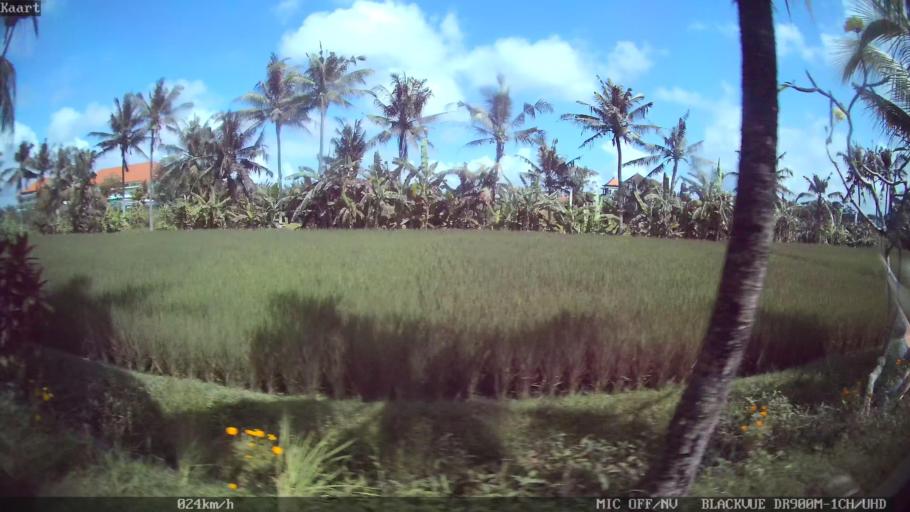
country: ID
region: Bali
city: Banjar Tebongkang
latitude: -8.5506
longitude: 115.2751
